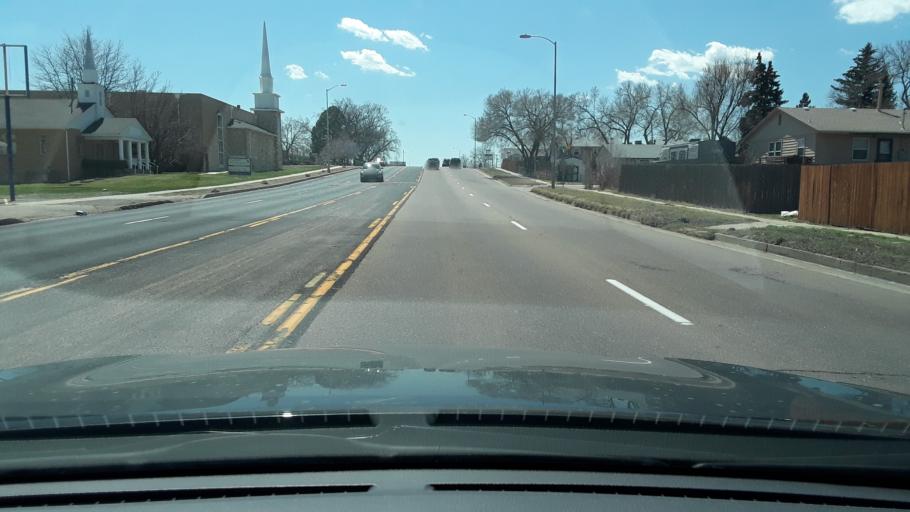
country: US
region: Colorado
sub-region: El Paso County
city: Colorado Springs
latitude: 38.8448
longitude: -104.7759
